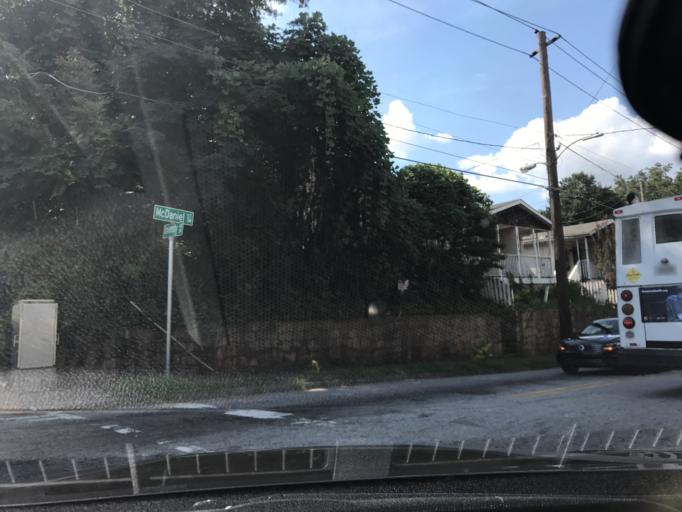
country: US
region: Georgia
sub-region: Fulton County
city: Atlanta
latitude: 33.7222
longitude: -84.4016
